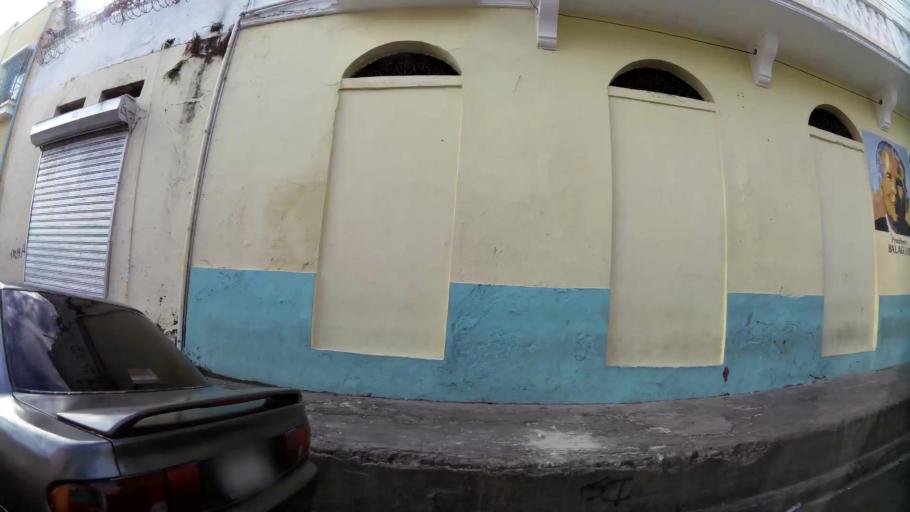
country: DO
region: Nacional
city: San Carlos
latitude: 18.4788
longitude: -69.8842
